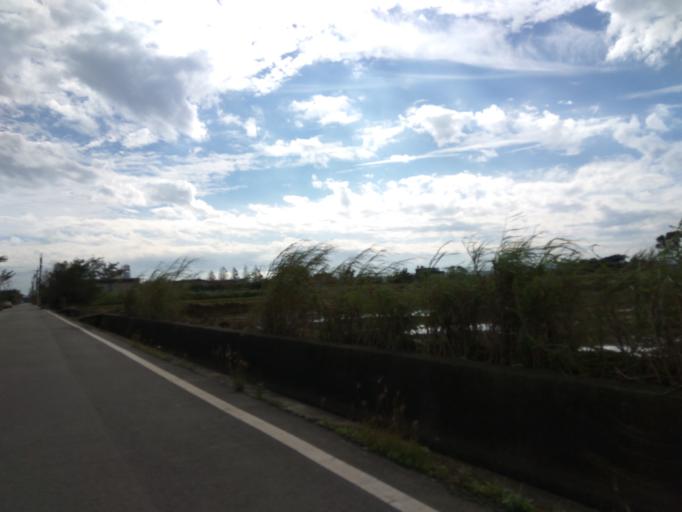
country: TW
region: Taiwan
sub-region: Hsinchu
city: Zhubei
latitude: 24.9536
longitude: 121.1066
